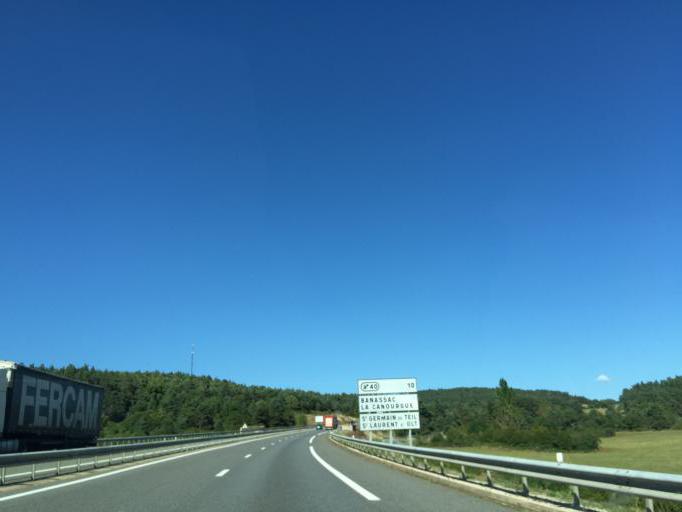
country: FR
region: Midi-Pyrenees
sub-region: Departement de l'Aveyron
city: Severac-le-Chateau
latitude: 44.3915
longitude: 3.1236
